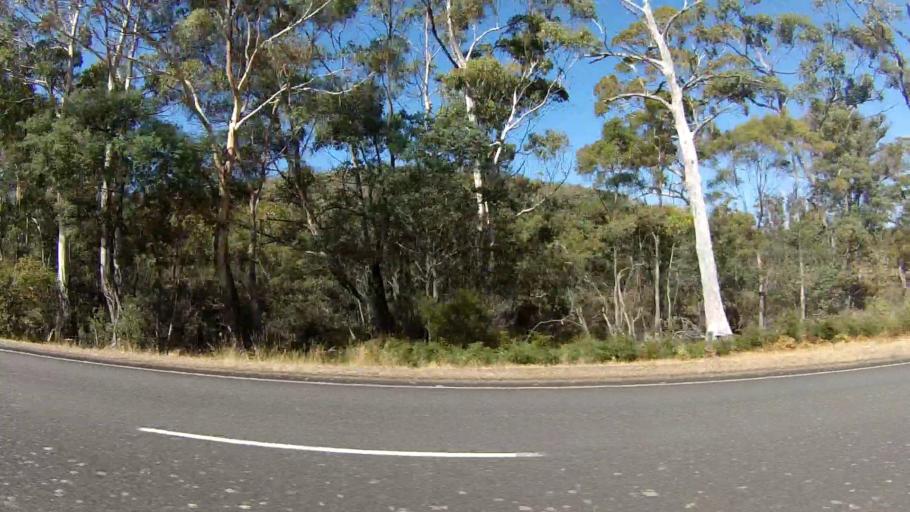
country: AU
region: Tasmania
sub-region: Sorell
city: Sorell
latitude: -42.5764
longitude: 147.8182
